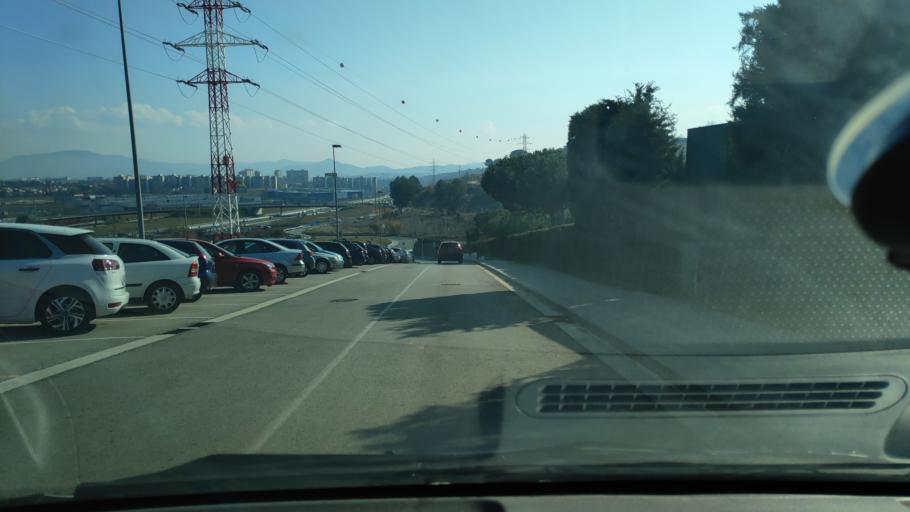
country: ES
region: Catalonia
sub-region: Provincia de Barcelona
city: Sant Quirze del Valles
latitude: 41.5149
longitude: 2.0964
